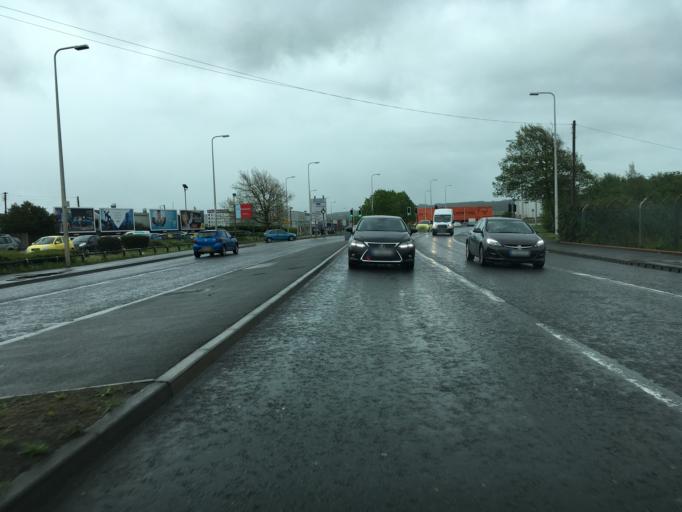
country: GB
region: England
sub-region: North Somerset
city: Weston-super-Mare
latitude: 51.3425
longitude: -2.9655
